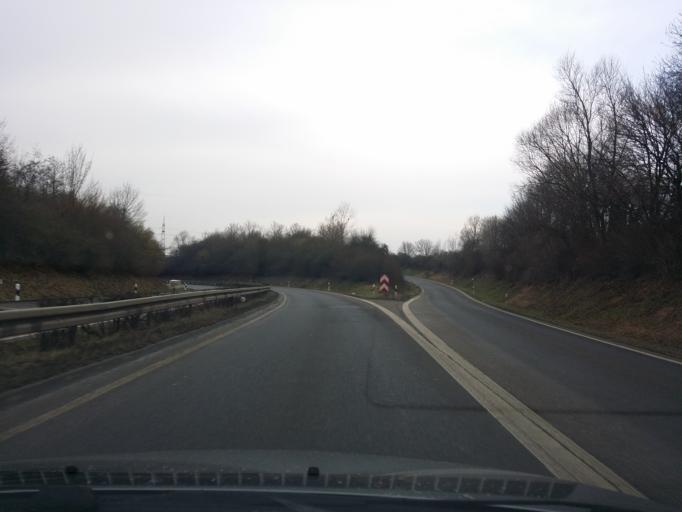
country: DE
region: Hesse
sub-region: Regierungsbezirk Darmstadt
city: Hochheim am Main
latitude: 50.0230
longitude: 8.3328
